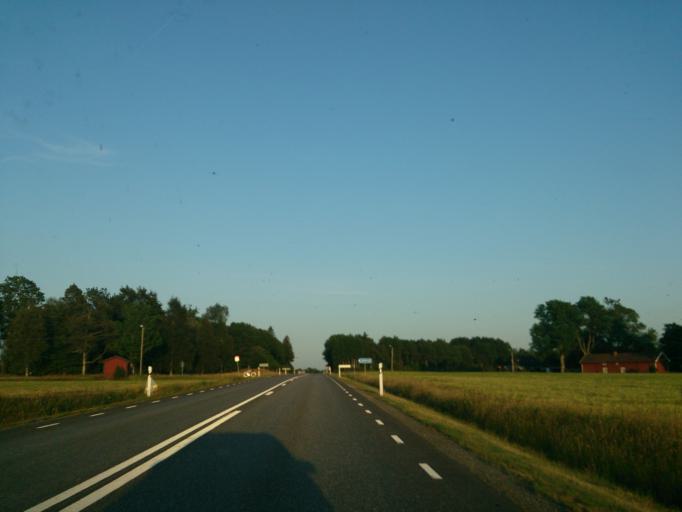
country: SE
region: Joenkoeping
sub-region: Varnamo Kommun
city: Rydaholm
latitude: 57.0019
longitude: 14.2728
